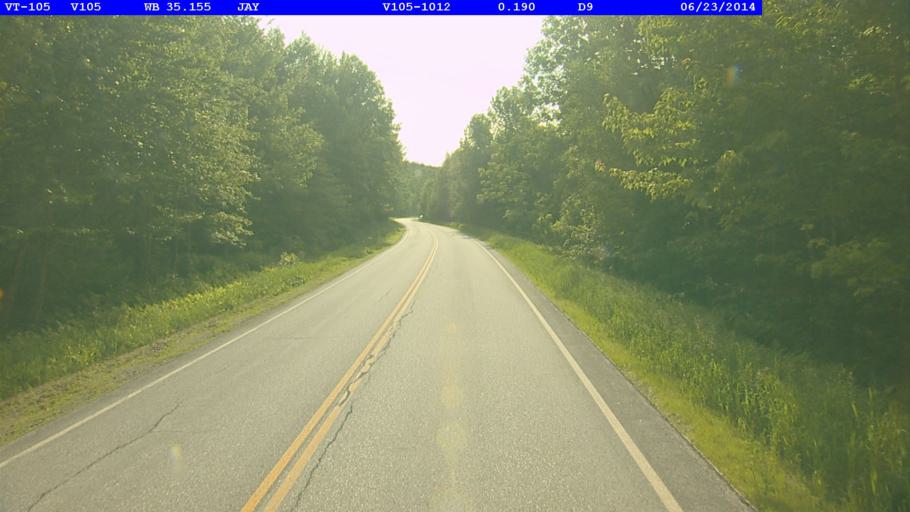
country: US
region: Vermont
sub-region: Franklin County
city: Richford
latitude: 44.9864
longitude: -72.5452
